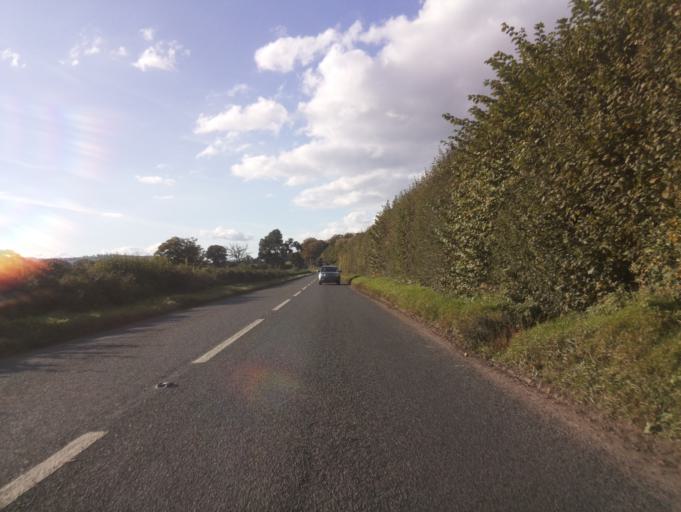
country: GB
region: England
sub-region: Herefordshire
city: Moccas
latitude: 52.0972
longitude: -2.9218
